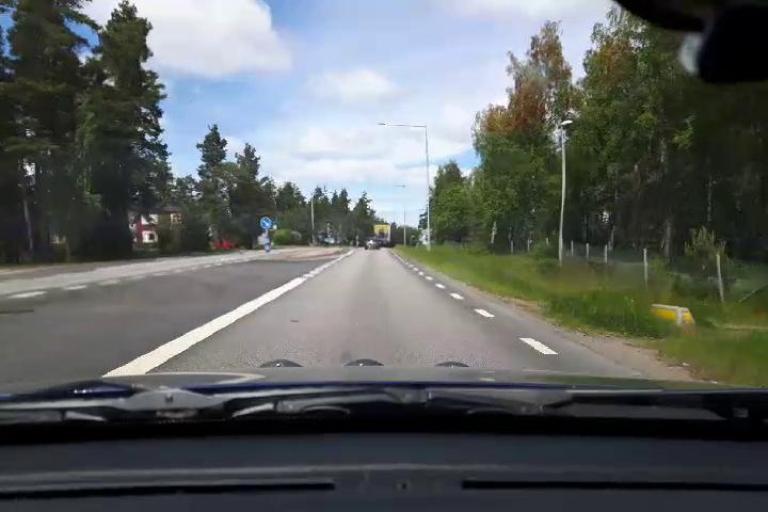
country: SE
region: Uppsala
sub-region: Osthammars Kommun
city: Bjorklinge
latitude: 60.0308
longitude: 17.5525
